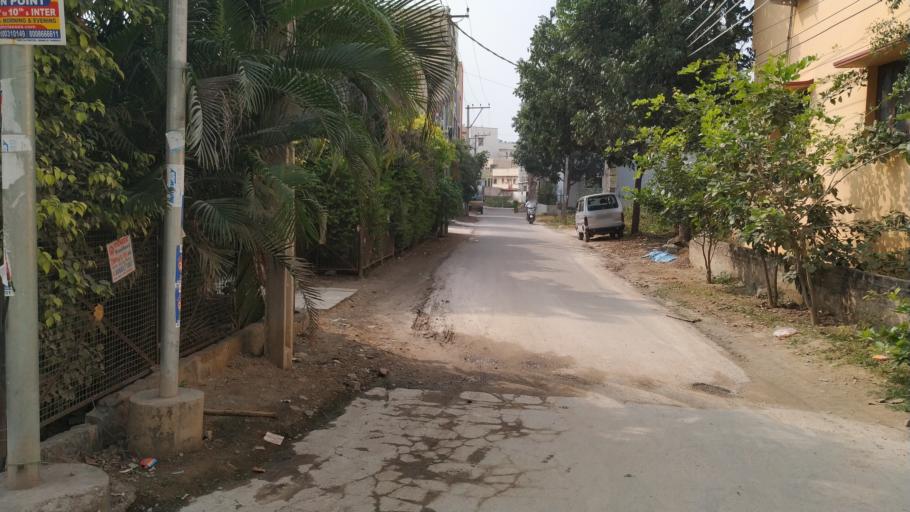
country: IN
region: Telangana
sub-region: Medak
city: Serilingampalle
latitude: 17.4928
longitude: 78.3196
